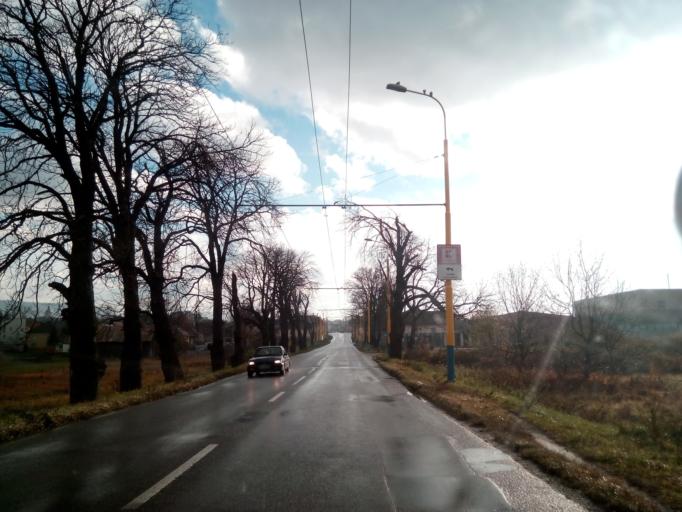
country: SK
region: Presovsky
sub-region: Okres Presov
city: Presov
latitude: 48.9803
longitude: 21.2587
